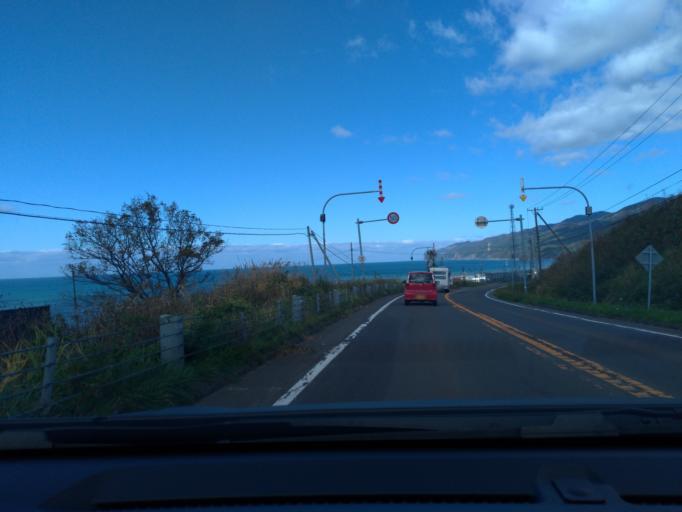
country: JP
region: Hokkaido
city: Ishikari
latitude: 43.3913
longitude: 141.4332
